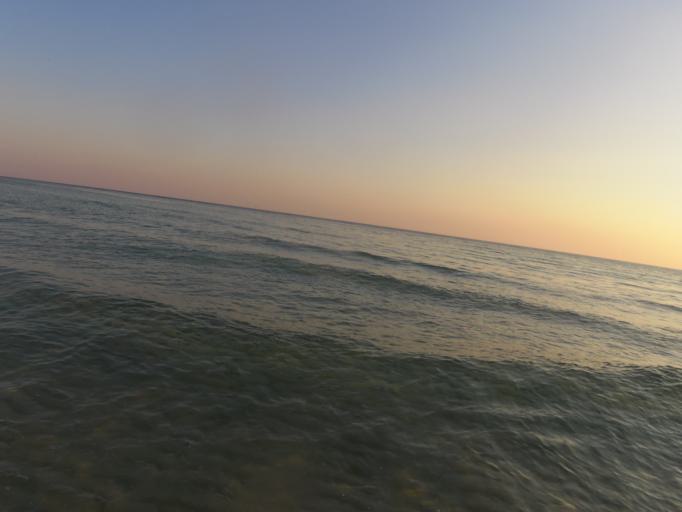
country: US
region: Florida
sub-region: Bay County
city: Laguna Beach
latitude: 30.2173
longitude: -85.8824
